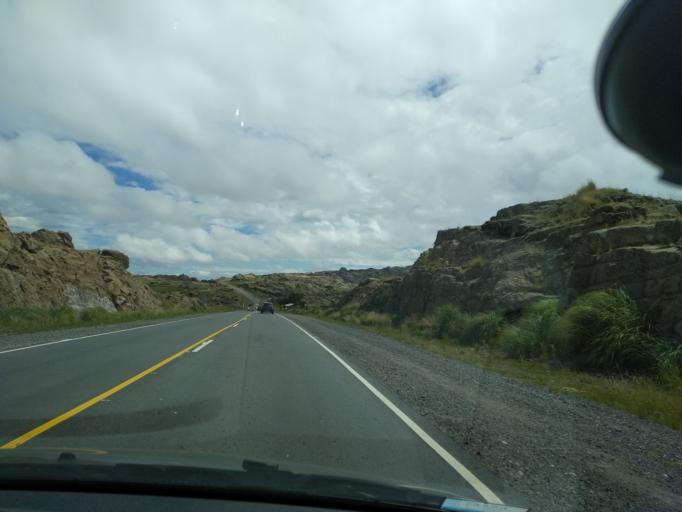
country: AR
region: Cordoba
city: Mina Clavero
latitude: -31.6947
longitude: -64.8954
